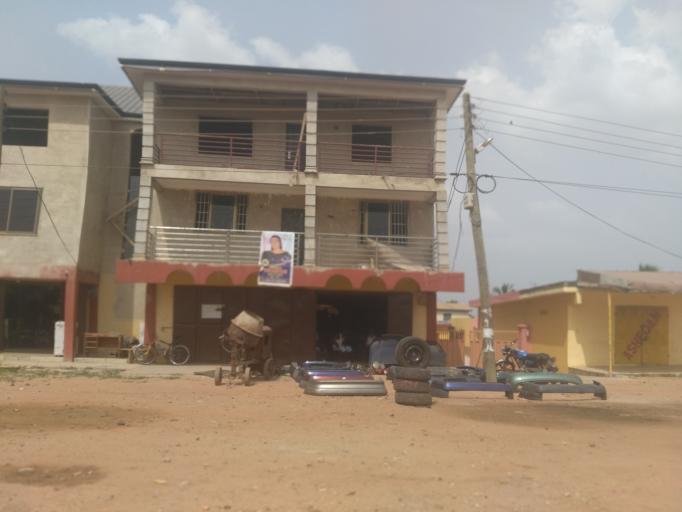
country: GH
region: Greater Accra
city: Gbawe
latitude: 5.5976
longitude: -0.2644
